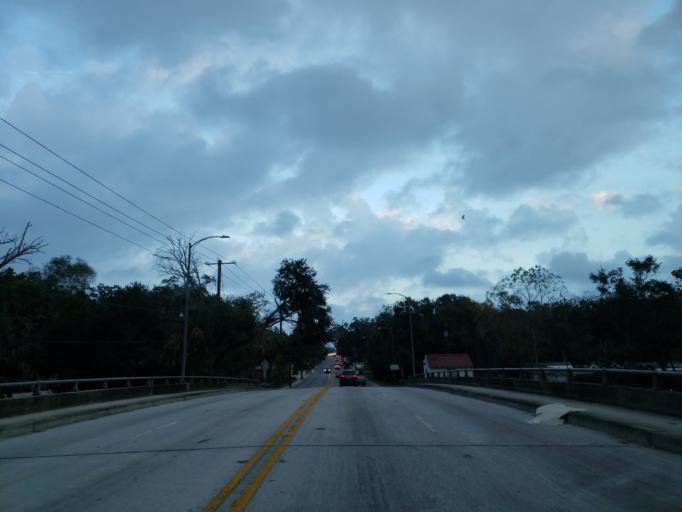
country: US
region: Florida
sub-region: Hillsborough County
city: Egypt Lake-Leto
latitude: 28.0107
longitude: -82.4651
